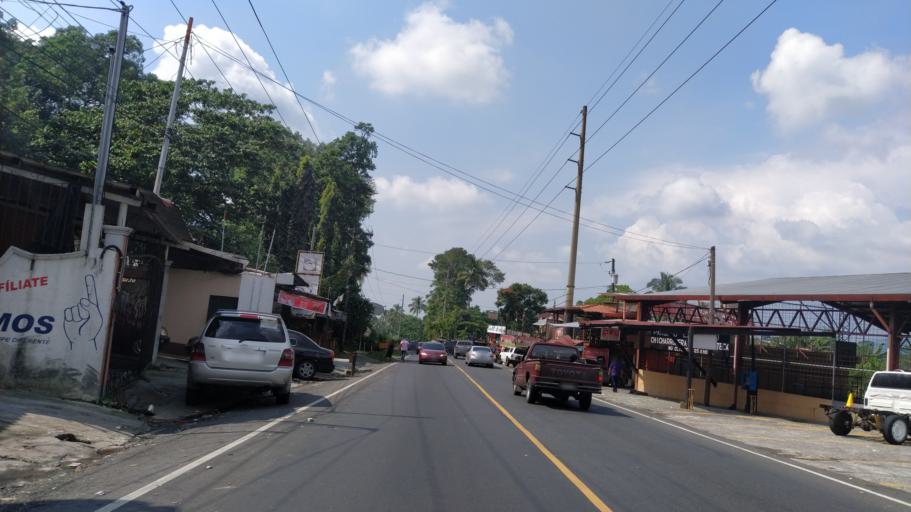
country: GT
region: Quetzaltenango
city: El Palmar
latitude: 14.6345
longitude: -91.5783
